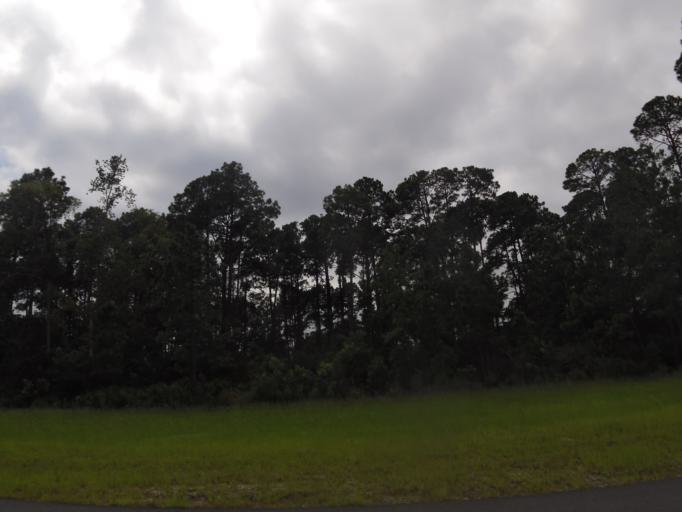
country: US
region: Georgia
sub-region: Glynn County
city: Brunswick
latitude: 31.1085
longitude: -81.5460
